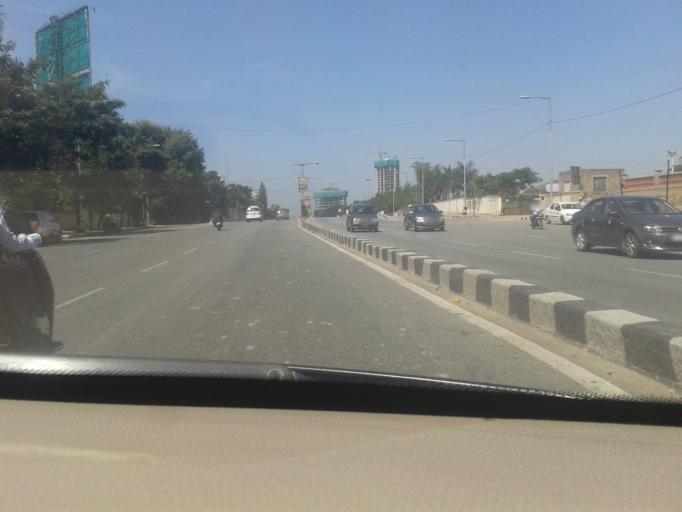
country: IN
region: Karnataka
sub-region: Bangalore Urban
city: Bangalore
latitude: 13.0103
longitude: 77.5838
